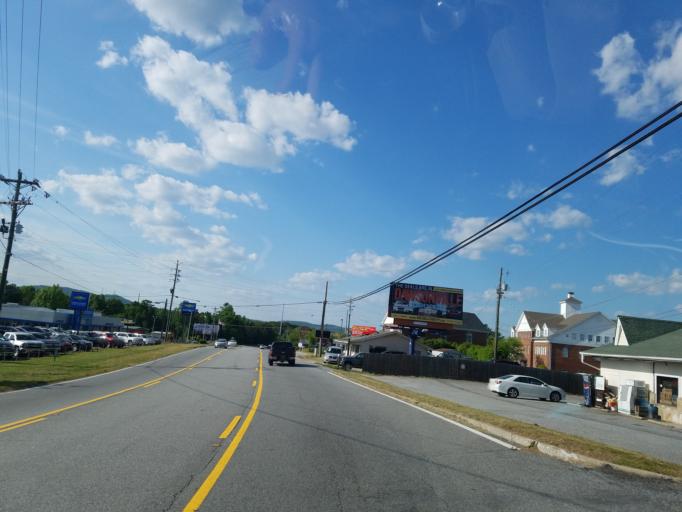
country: US
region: Georgia
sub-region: Forsyth County
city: Cumming
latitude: 34.1931
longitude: -84.1355
